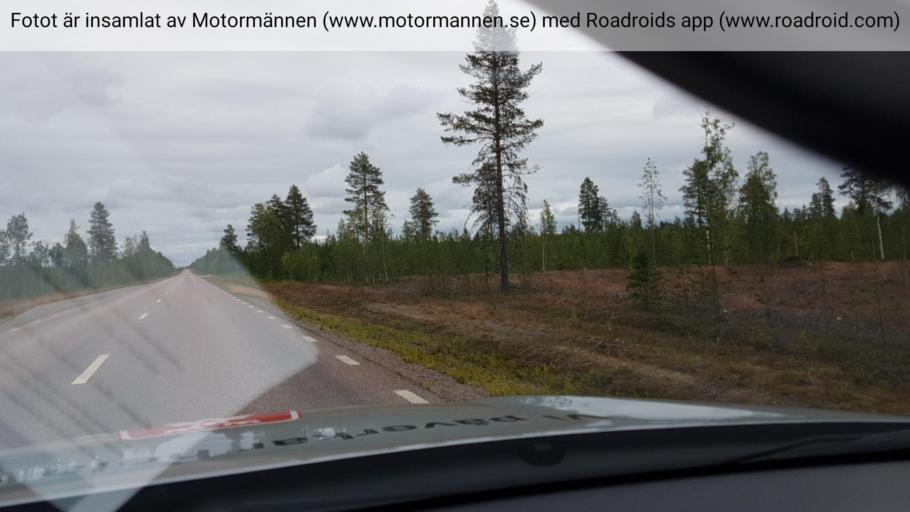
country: SE
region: Norrbotten
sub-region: Overkalix Kommun
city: OEverkalix
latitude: 67.0876
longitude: 22.5569
